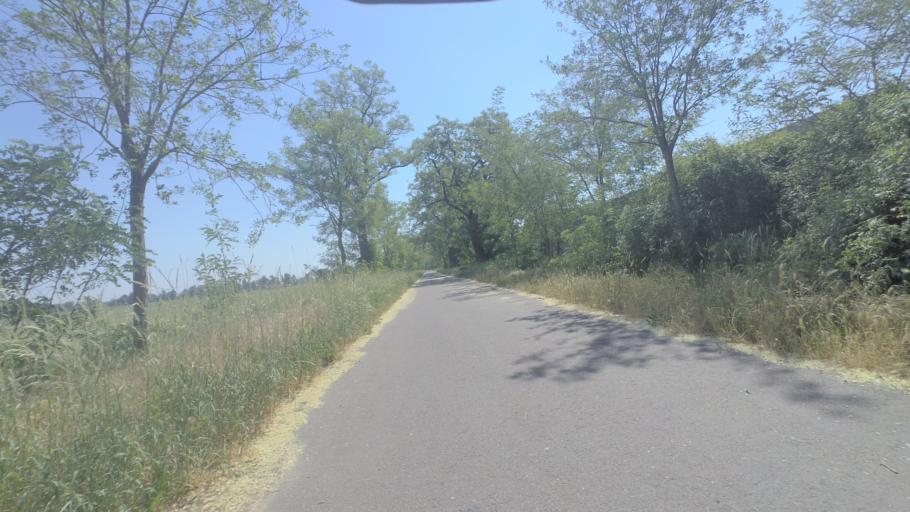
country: DE
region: Saxony-Anhalt
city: Oranienbaum
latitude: 51.7967
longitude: 12.4150
